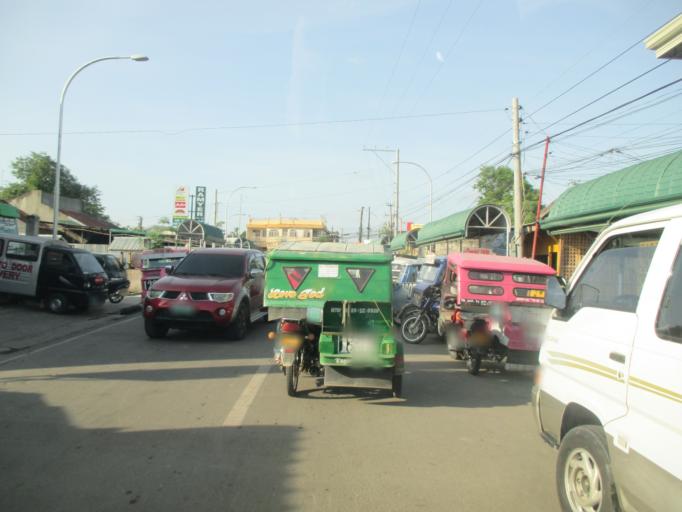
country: PH
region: Central Visayas
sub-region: Province of Bohol
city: Tagbilaran City
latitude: 9.6567
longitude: 123.8532
